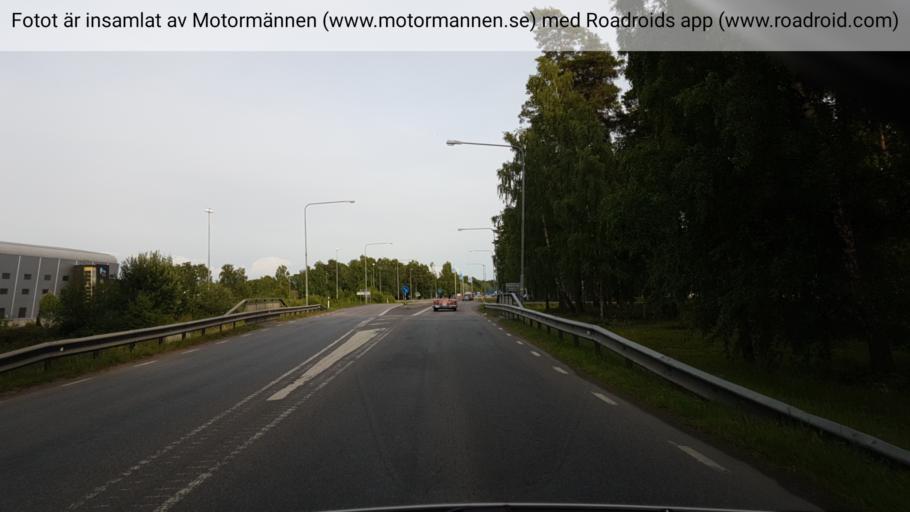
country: SE
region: Vaestra Goetaland
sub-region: Lidkopings Kommun
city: Lidkoping
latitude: 58.4945
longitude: 13.1389
